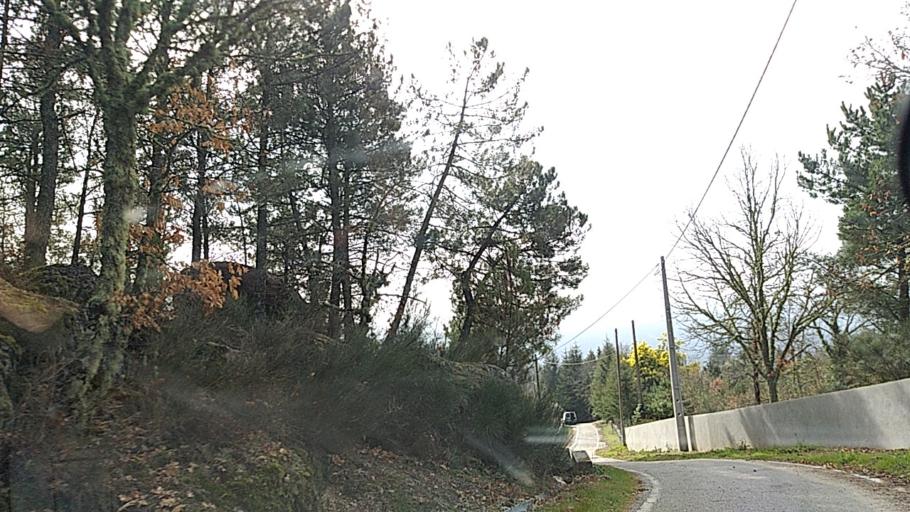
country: PT
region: Guarda
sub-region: Fornos de Algodres
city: Fornos de Algodres
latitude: 40.6340
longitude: -7.5380
